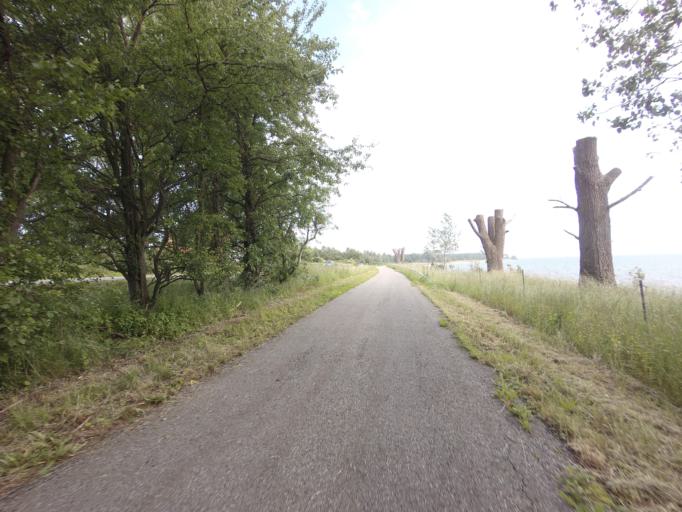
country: SE
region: Skane
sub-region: Ystads Kommun
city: Ystad
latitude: 55.4265
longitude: 13.7544
